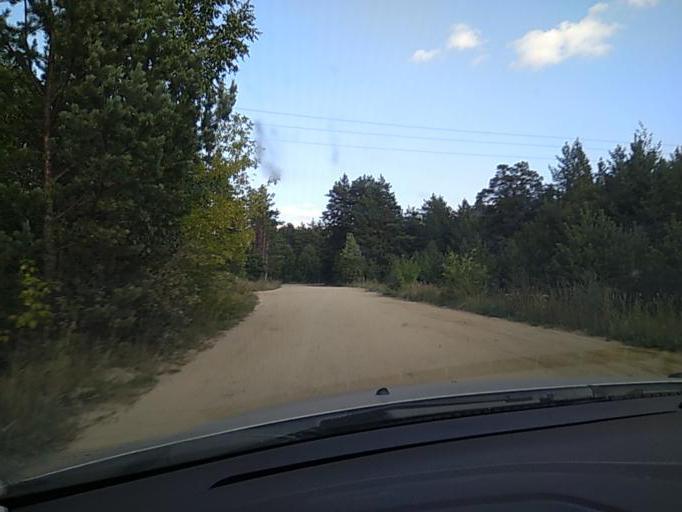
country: RU
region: Chelyabinsk
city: Kyshtym
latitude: 55.6860
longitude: 60.5653
